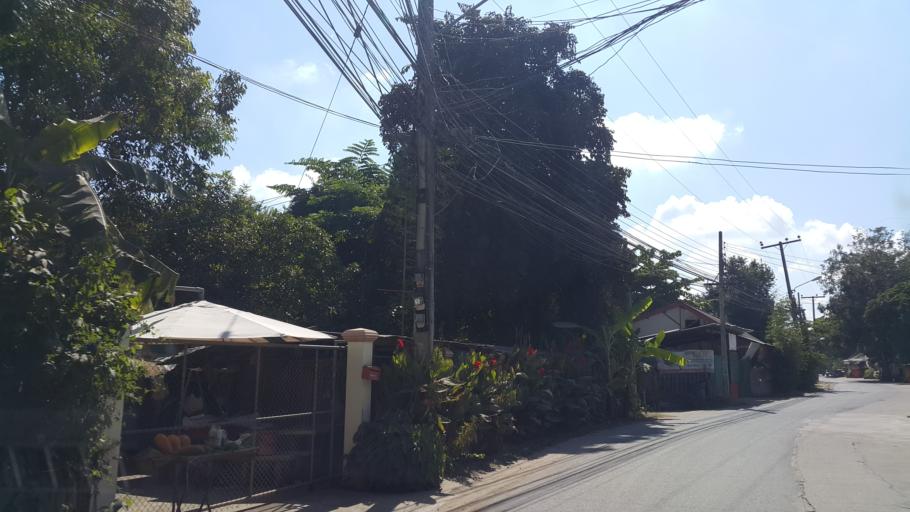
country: TH
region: Chiang Mai
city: San Sai
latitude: 18.8342
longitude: 99.0203
